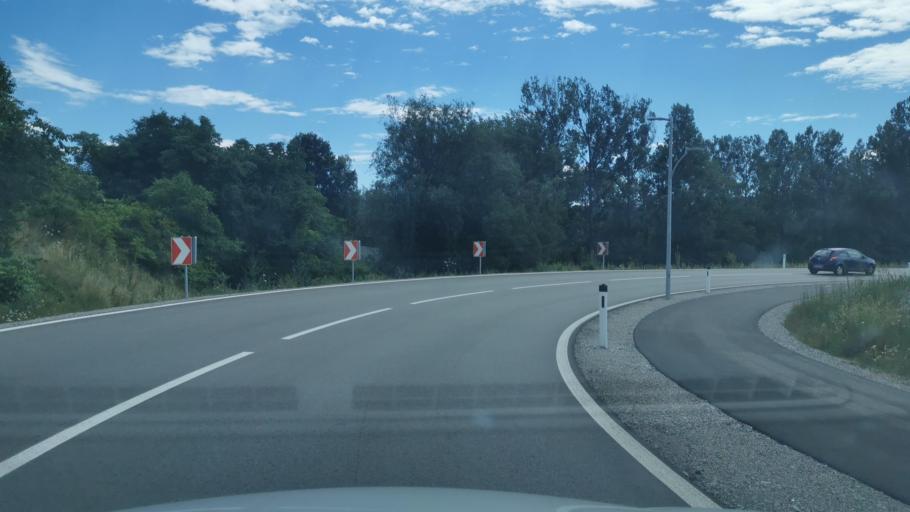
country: AT
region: Lower Austria
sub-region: Politischer Bezirk Sankt Polten
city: Wilhelmsburg
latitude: 48.1313
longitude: 15.6163
